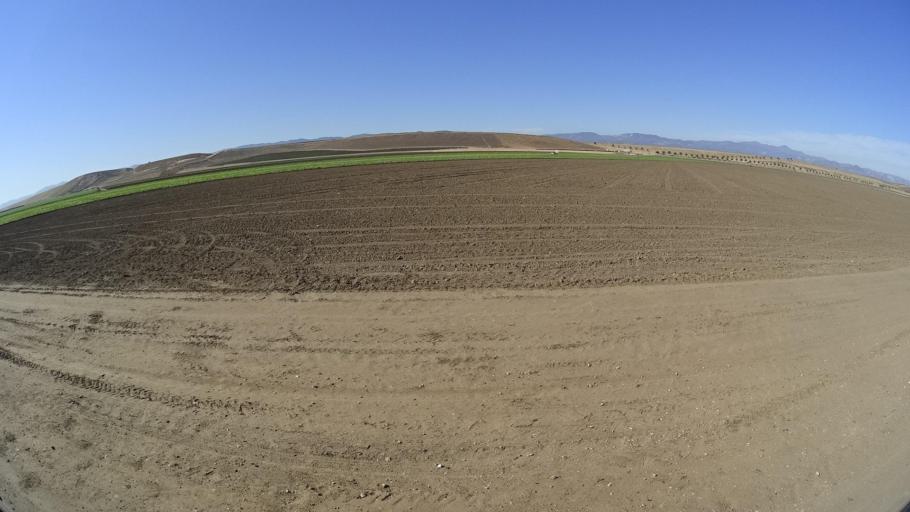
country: US
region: California
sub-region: Monterey County
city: King City
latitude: 36.1577
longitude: -121.0198
